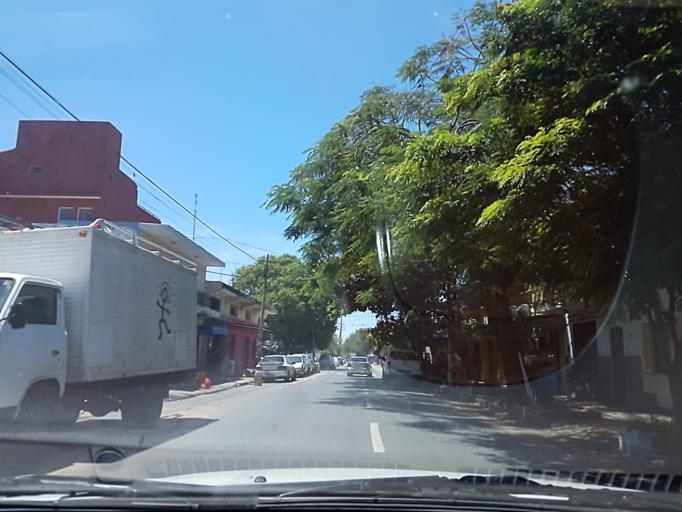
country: PY
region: Asuncion
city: Asuncion
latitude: -25.3070
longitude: -57.6064
